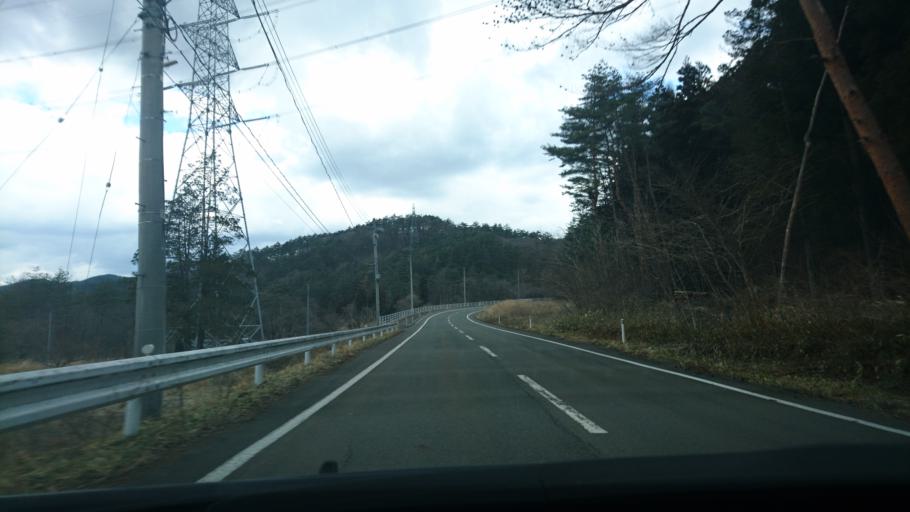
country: JP
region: Iwate
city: Tono
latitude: 39.3449
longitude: 141.3349
